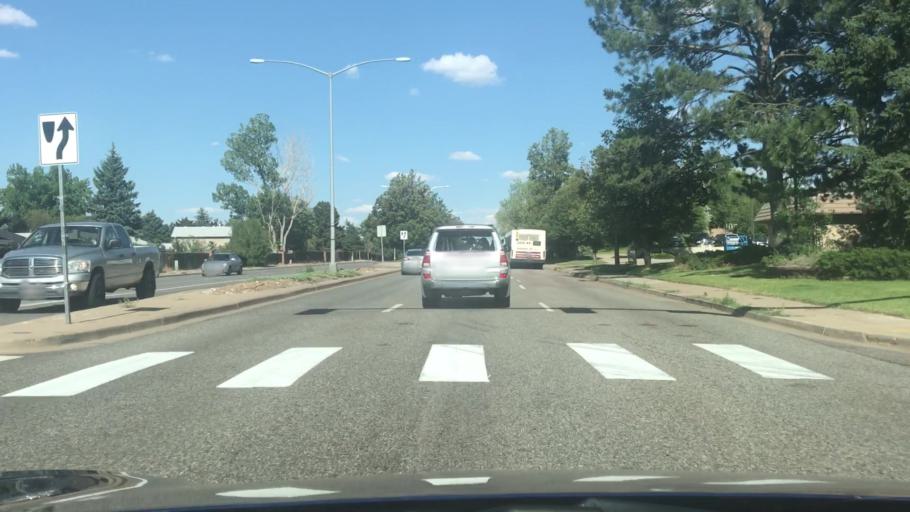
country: US
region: Colorado
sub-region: Arapahoe County
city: Dove Valley
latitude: 39.6530
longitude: -104.8072
